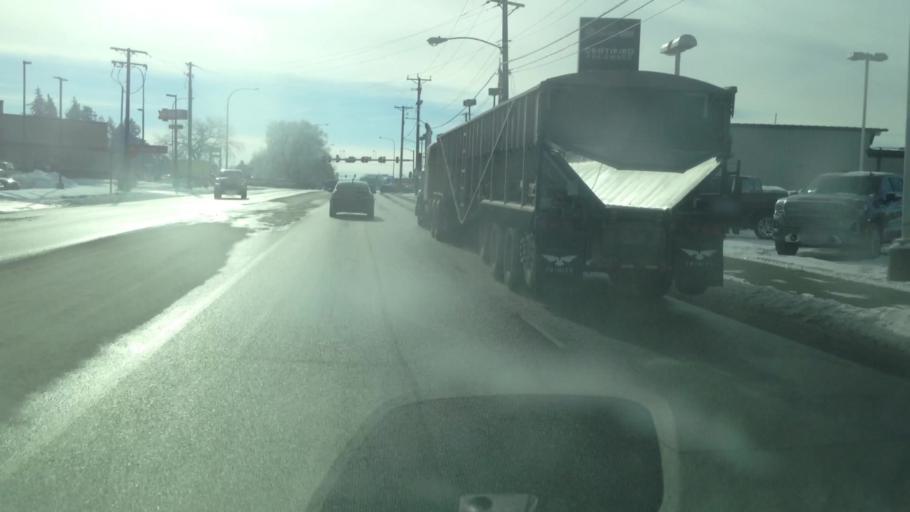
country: US
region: Idaho
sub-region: Bonneville County
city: Idaho Falls
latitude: 43.5081
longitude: -112.0238
